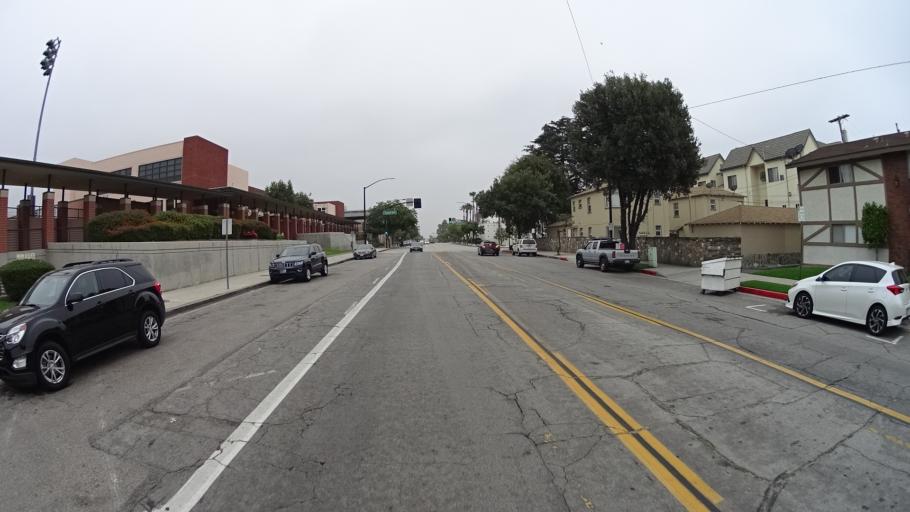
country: US
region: California
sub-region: Los Angeles County
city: Burbank
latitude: 34.1879
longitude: -118.3154
